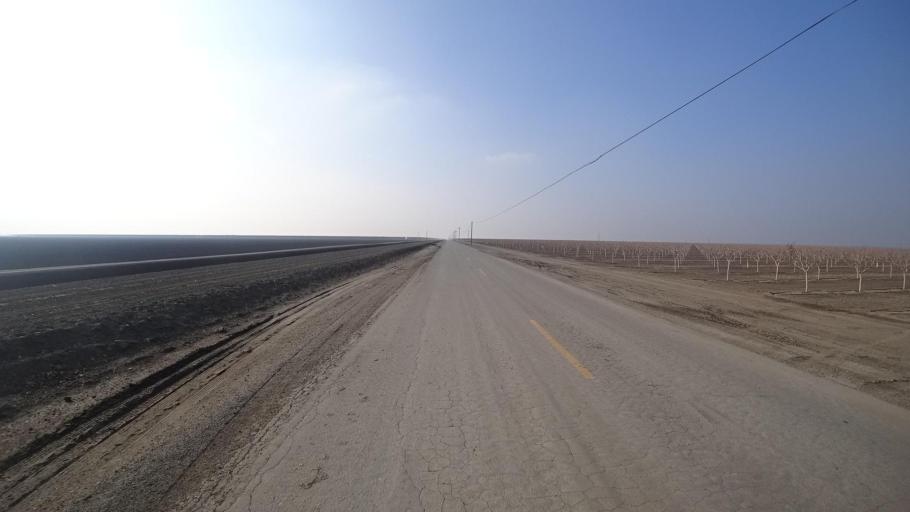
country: US
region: California
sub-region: Kern County
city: Greenfield
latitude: 35.1514
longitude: -119.0521
